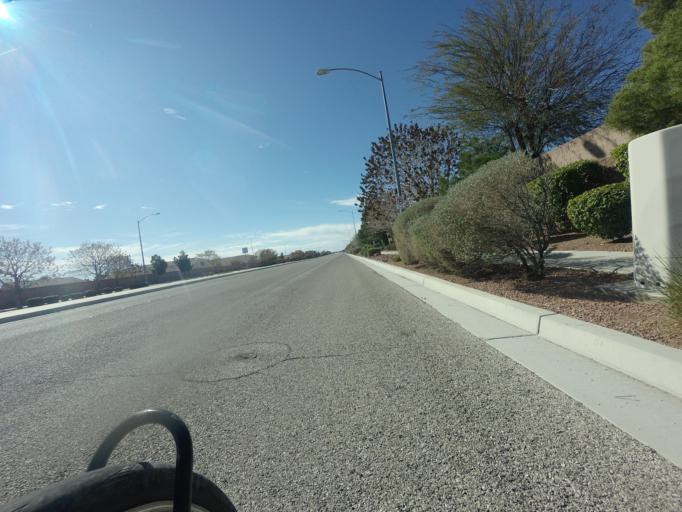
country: US
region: Nevada
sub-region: Clark County
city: North Las Vegas
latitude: 36.3340
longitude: -115.2788
